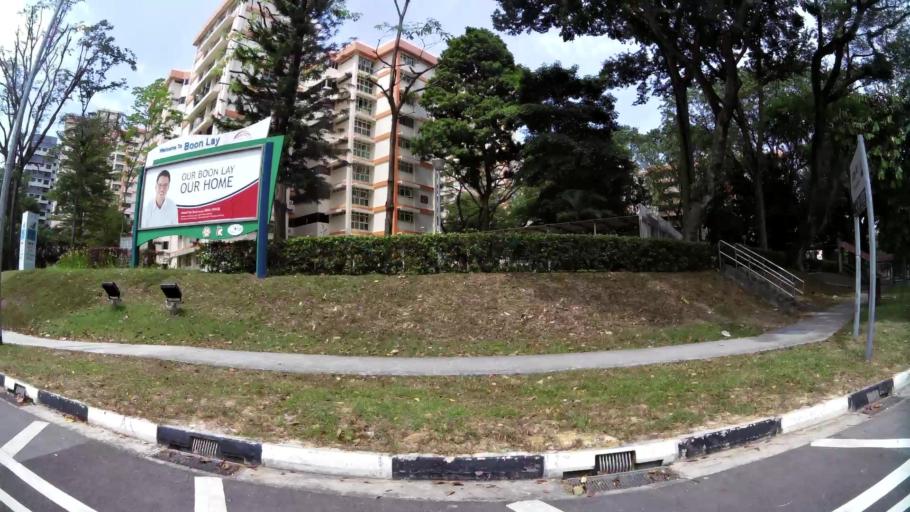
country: MY
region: Johor
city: Johor Bahru
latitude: 1.3431
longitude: 103.7159
